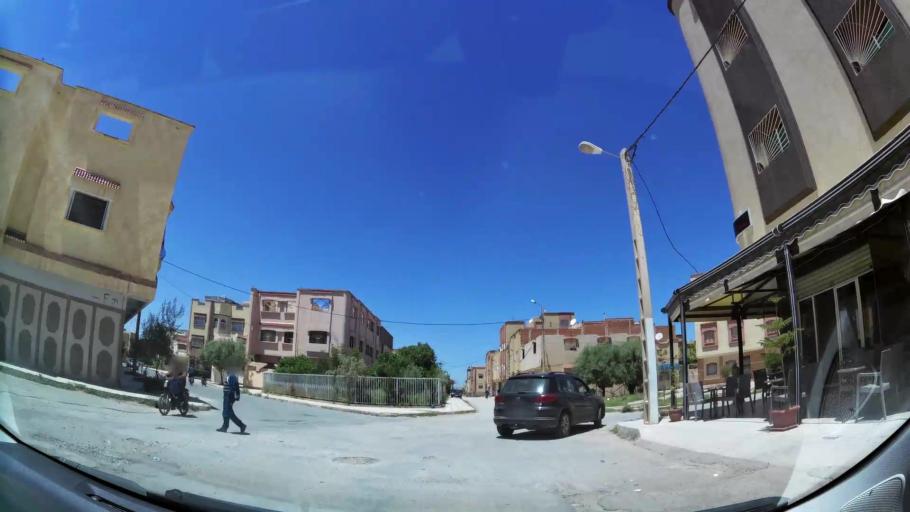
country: MA
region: Oriental
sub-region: Oujda-Angad
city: Oujda
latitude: 34.6796
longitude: -1.8741
